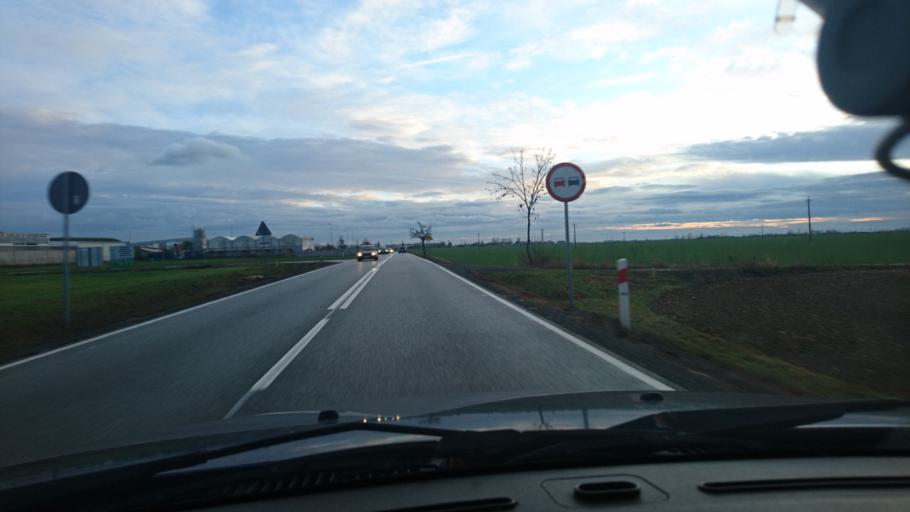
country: PL
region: Opole Voivodeship
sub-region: Powiat kluczborski
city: Kluczbork
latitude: 51.0047
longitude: 18.2049
